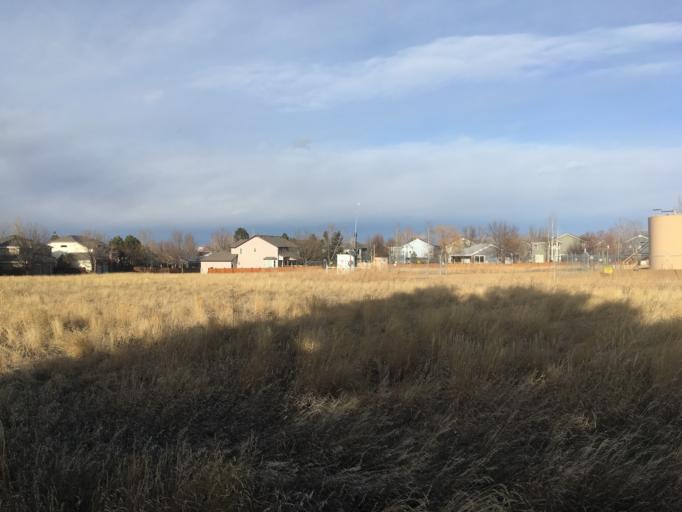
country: US
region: Colorado
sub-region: Boulder County
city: Lafayette
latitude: 40.0162
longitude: -105.0870
